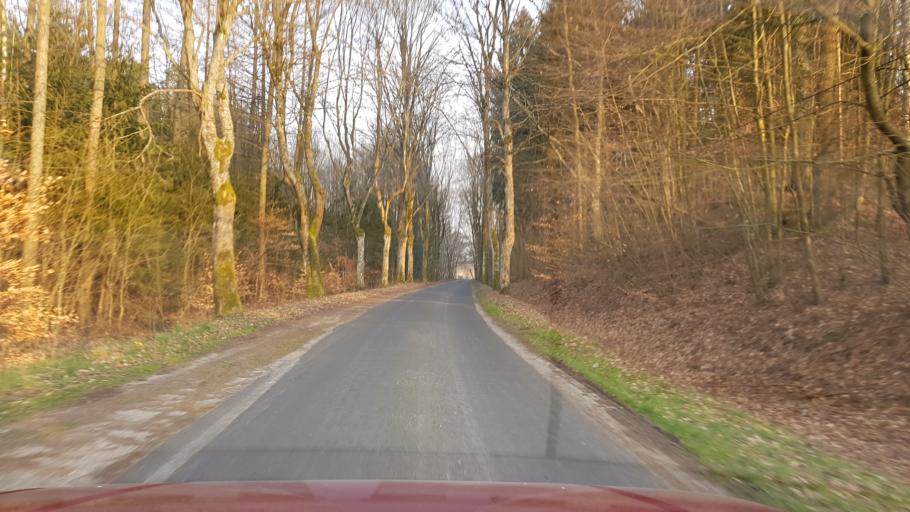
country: PL
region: West Pomeranian Voivodeship
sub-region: Powiat swidwinski
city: Swidwin
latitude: 53.7348
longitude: 15.7229
